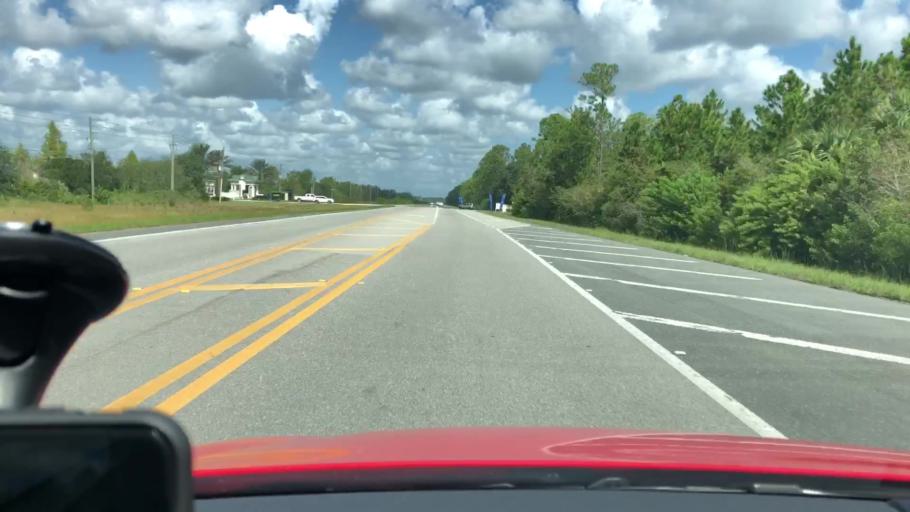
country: US
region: Florida
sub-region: Volusia County
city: Holly Hill
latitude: 29.1894
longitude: -81.1197
